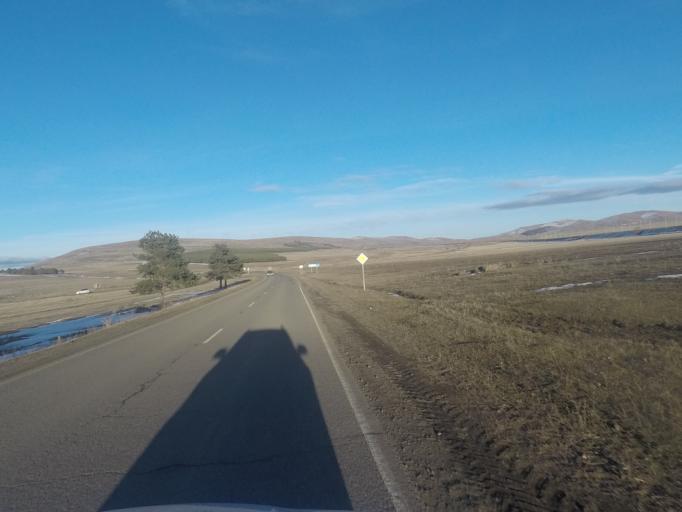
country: GE
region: Kvemo Kartli
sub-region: Tsalka
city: Tsalka
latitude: 41.6186
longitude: 44.1374
